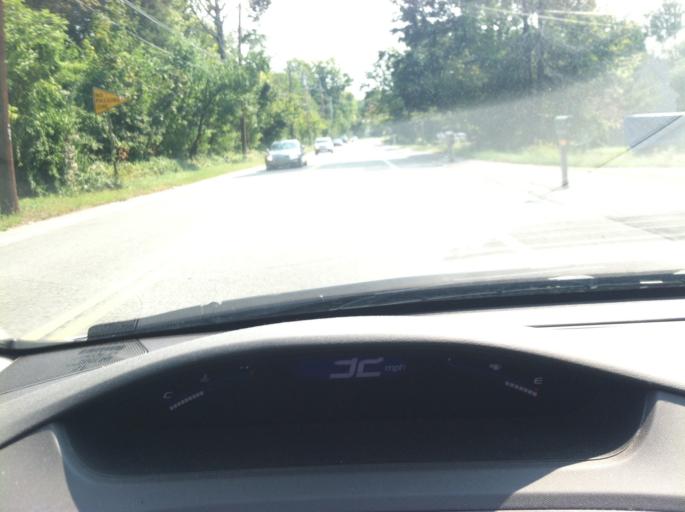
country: US
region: Massachusetts
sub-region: Middlesex County
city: Bedford
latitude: 42.5007
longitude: -71.2843
